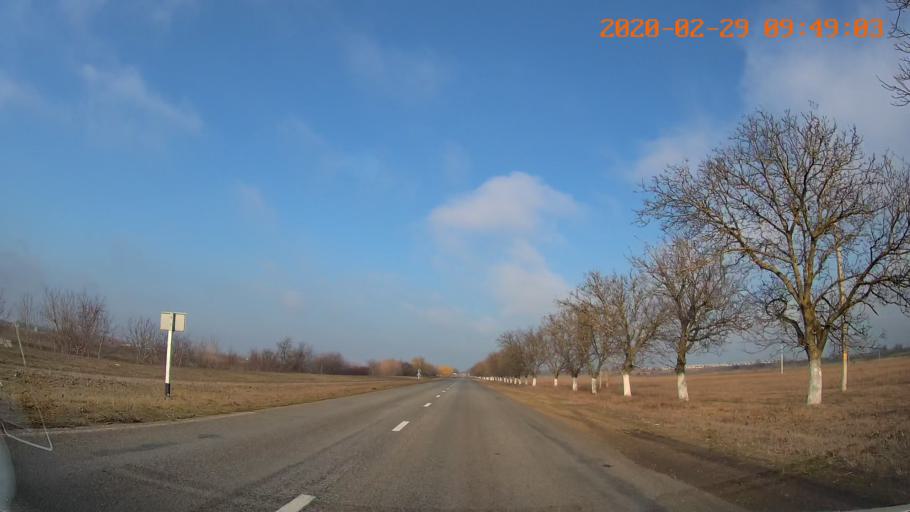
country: MD
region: Telenesti
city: Crasnoe
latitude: 46.6943
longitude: 29.7781
